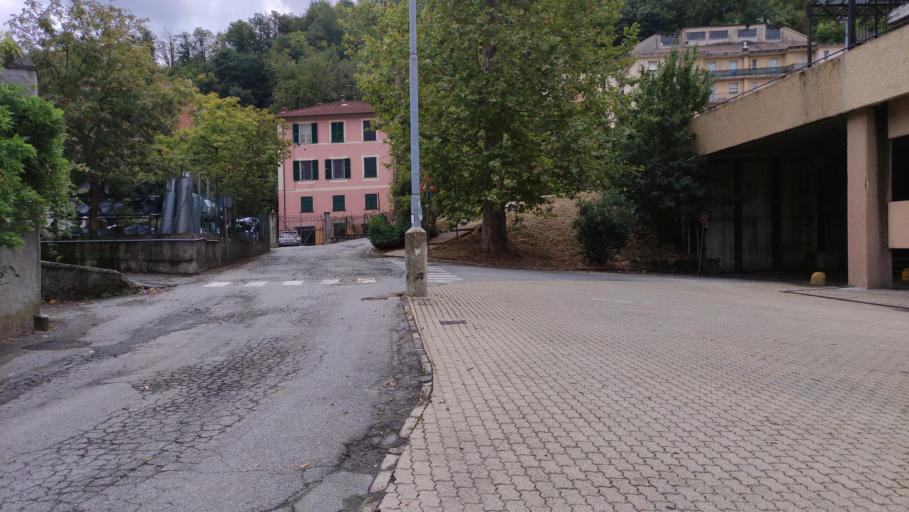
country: IT
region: Liguria
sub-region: Provincia di Genova
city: Busalla
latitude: 44.5673
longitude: 8.9628
